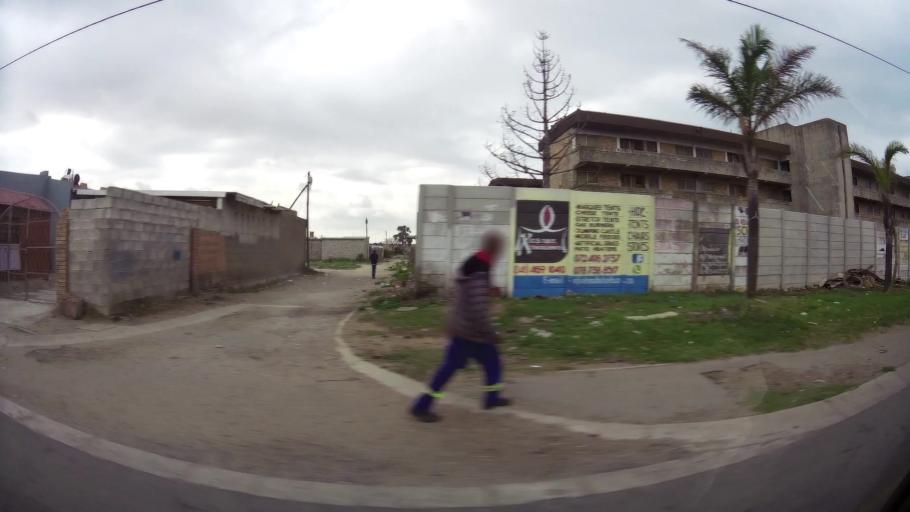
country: ZA
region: Eastern Cape
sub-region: Nelson Mandela Bay Metropolitan Municipality
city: Port Elizabeth
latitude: -33.9075
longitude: 25.6027
